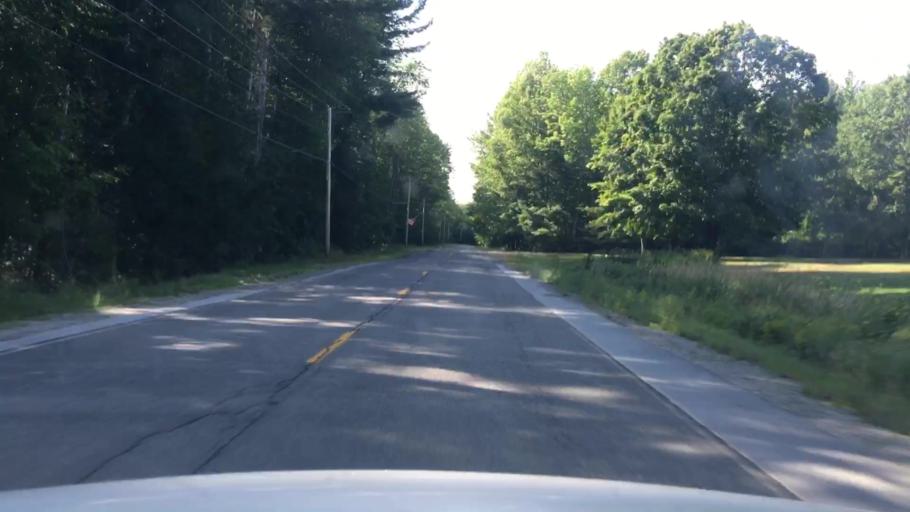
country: US
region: Maine
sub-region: Penobscot County
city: Enfield
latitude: 45.2159
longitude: -68.5301
